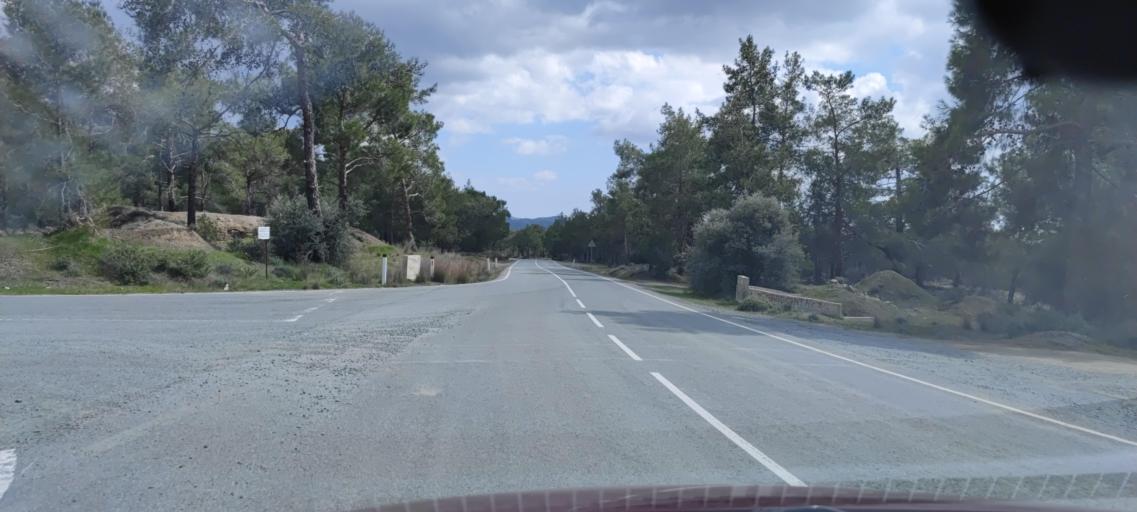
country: CY
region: Lefkosia
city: Lythrodontas
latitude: 34.9287
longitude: 33.3415
